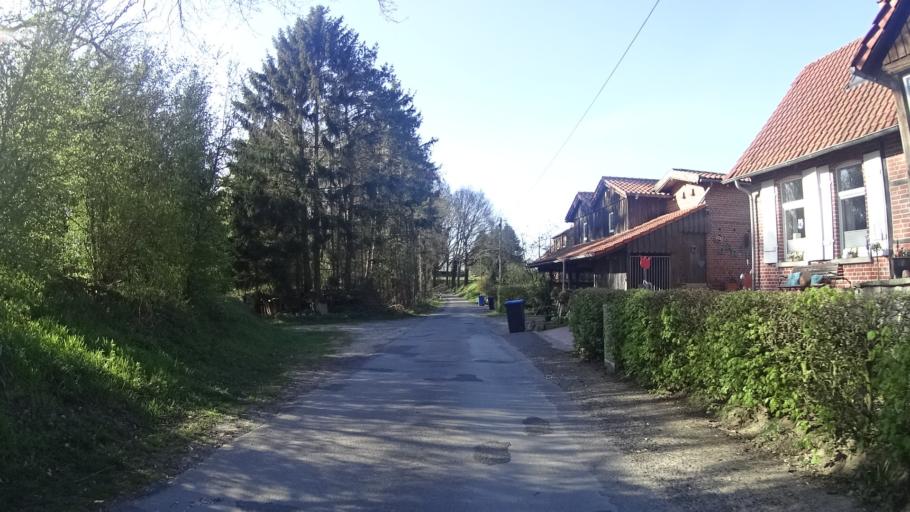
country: DE
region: North Rhine-Westphalia
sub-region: Regierungsbezirk Munster
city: Greven
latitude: 52.0785
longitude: 7.6044
